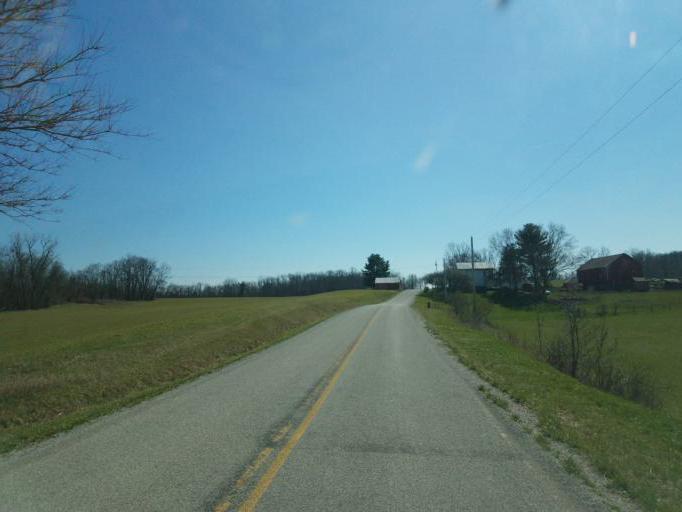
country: US
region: Ohio
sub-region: Richland County
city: Lincoln Heights
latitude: 40.7960
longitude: -82.3916
